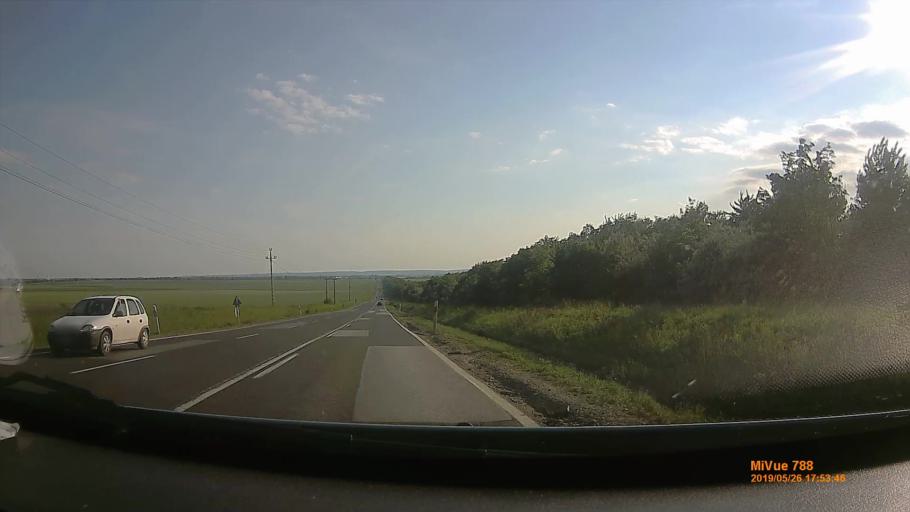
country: HU
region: Borsod-Abauj-Zemplen
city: Arnot
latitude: 48.1492
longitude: 20.8934
